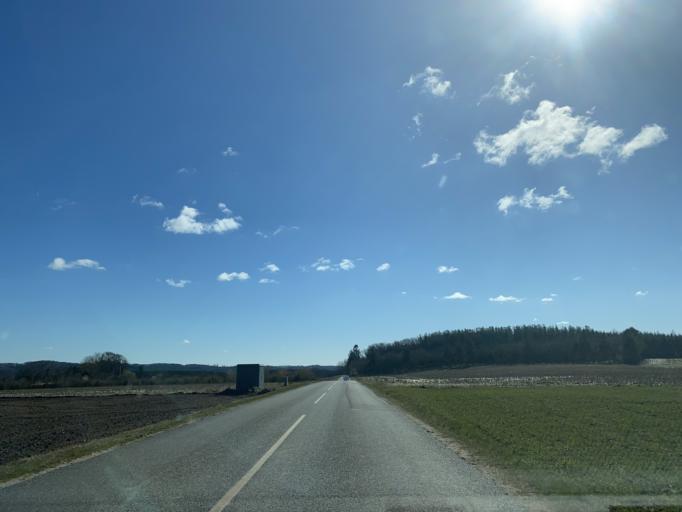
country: DK
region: Central Jutland
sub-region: Silkeborg Kommune
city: Svejbaek
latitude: 56.2483
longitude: 9.6549
